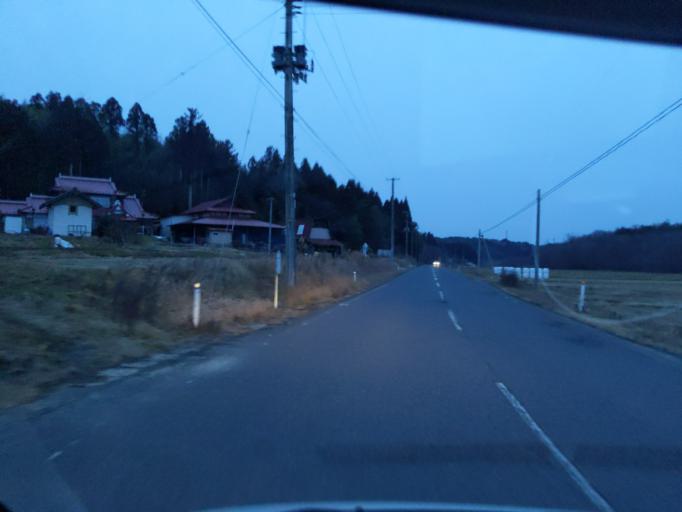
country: JP
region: Iwate
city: Ichinoseki
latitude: 38.8258
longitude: 141.1176
